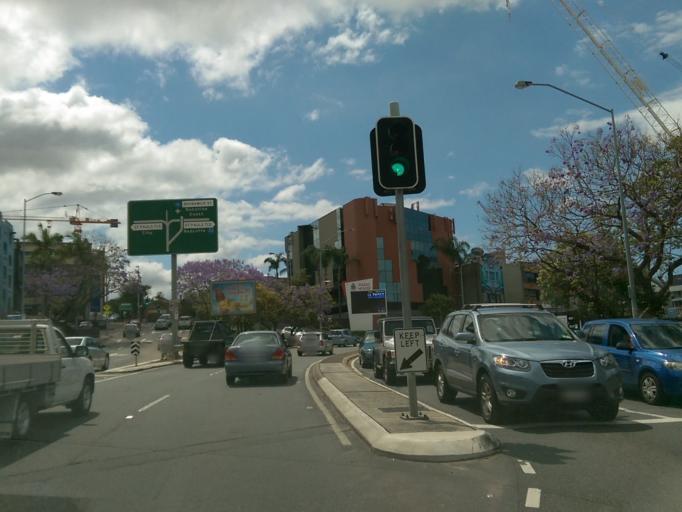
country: AU
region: Queensland
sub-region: Brisbane
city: Fortitude Valley
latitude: -27.4579
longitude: 153.0315
